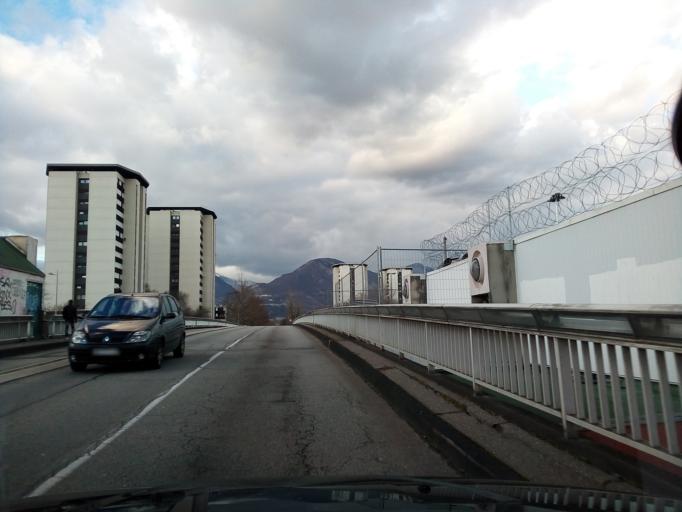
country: FR
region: Rhone-Alpes
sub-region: Departement de l'Isere
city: Echirolles
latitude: 45.1583
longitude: 5.7289
